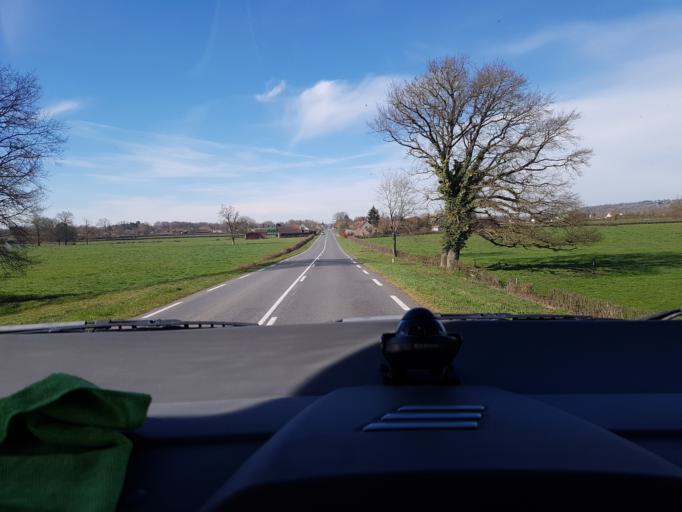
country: FR
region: Bourgogne
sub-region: Departement de Saone-et-Loire
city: Digoin
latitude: 46.5055
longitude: 4.0219
